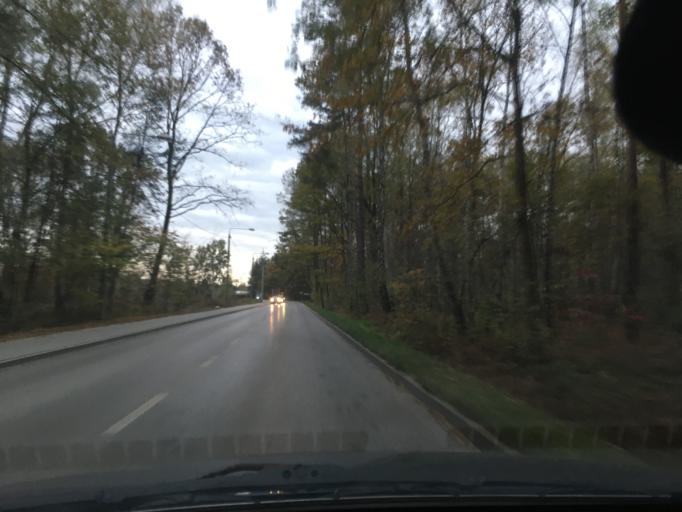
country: PL
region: Masovian Voivodeship
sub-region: Powiat piaseczynski
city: Lesznowola
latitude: 52.0787
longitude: 20.9374
